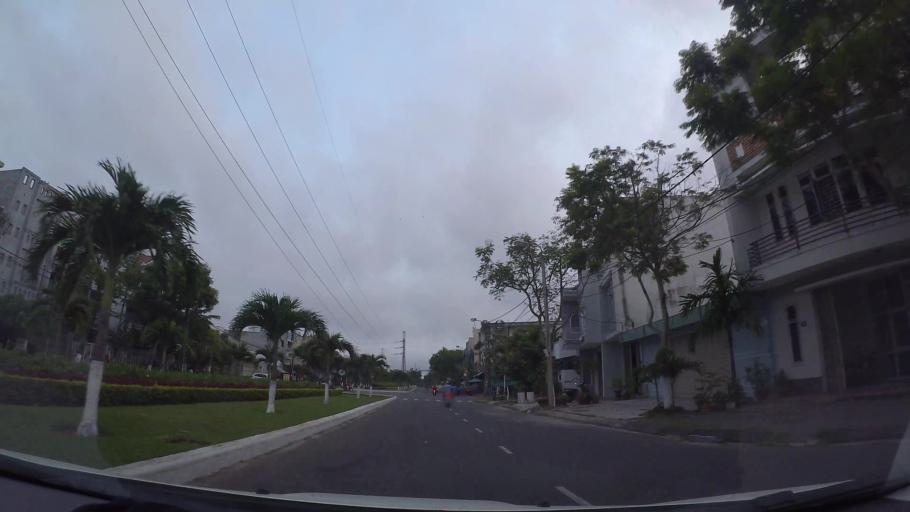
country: VN
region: Da Nang
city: Son Tra
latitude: 16.0412
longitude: 108.2384
